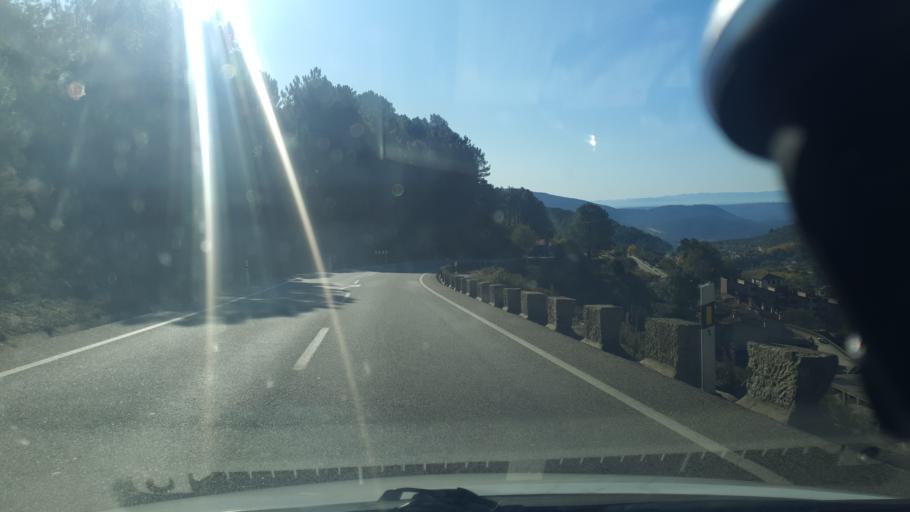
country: ES
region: Castille and Leon
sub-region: Provincia de Avila
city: Cuevas del Valle
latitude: 40.2988
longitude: -5.0071
